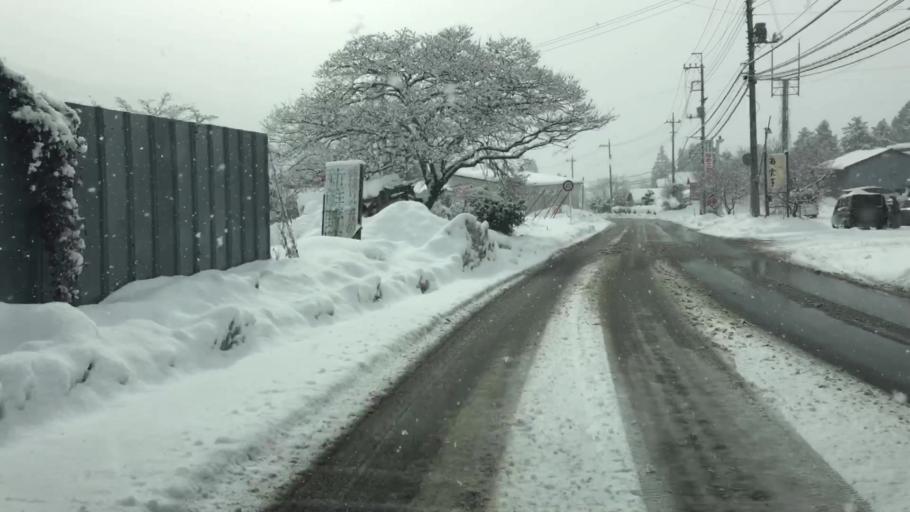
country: JP
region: Gunma
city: Numata
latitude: 36.7171
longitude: 139.0648
